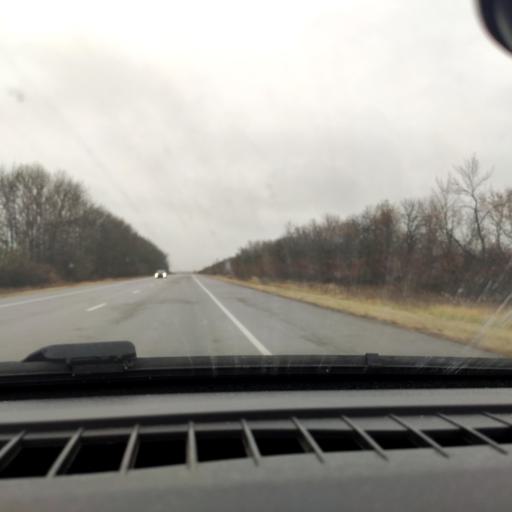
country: RU
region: Voronezj
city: Kolodeznyy
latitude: 51.2973
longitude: 39.0398
